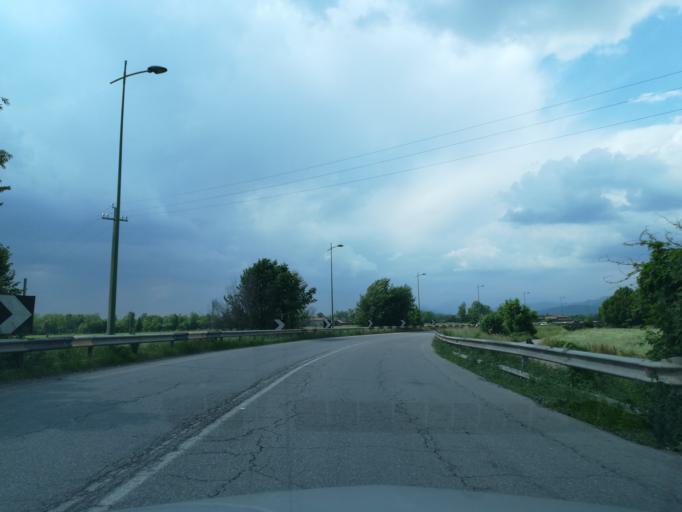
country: IT
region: Lombardy
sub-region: Provincia di Bergamo
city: Cavernago
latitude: 45.6428
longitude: 9.7471
